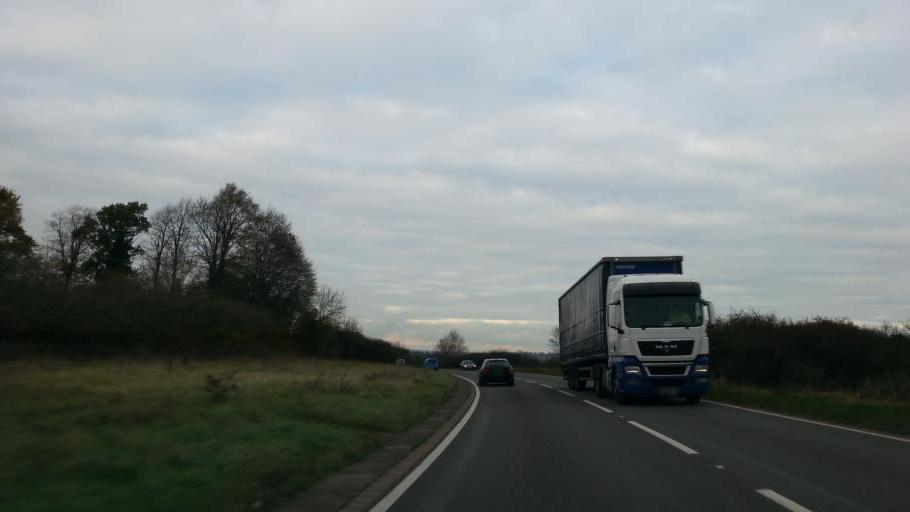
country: GB
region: England
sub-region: District of Rutland
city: Ketton
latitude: 52.5807
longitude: -0.5614
